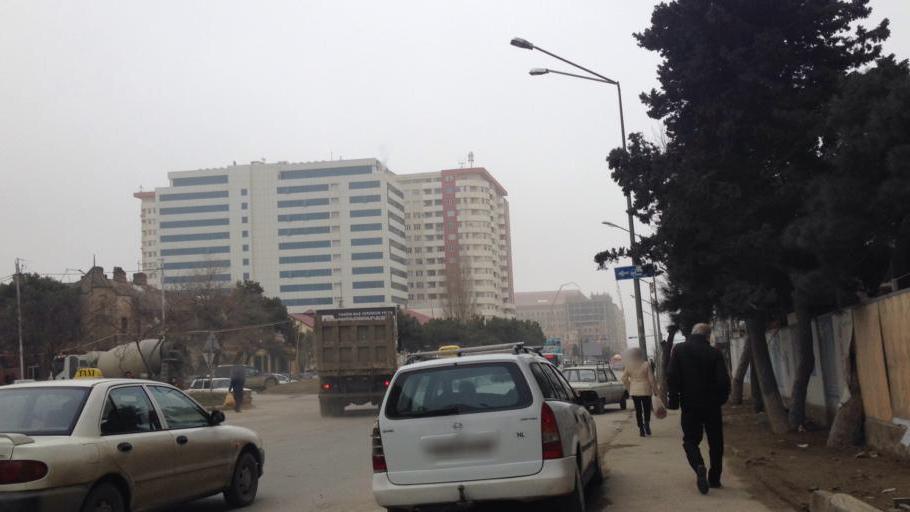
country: AZ
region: Baki
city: Baku
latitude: 40.3851
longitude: 49.8764
